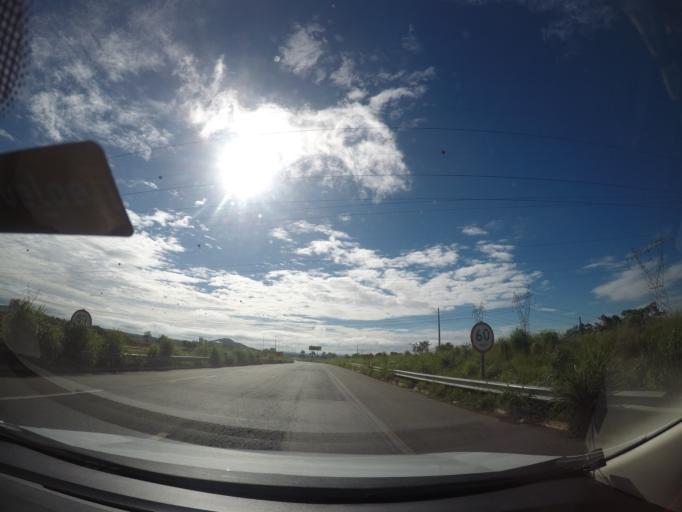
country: BR
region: Goias
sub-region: Senador Canedo
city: Senador Canedo
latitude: -16.6860
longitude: -49.1579
